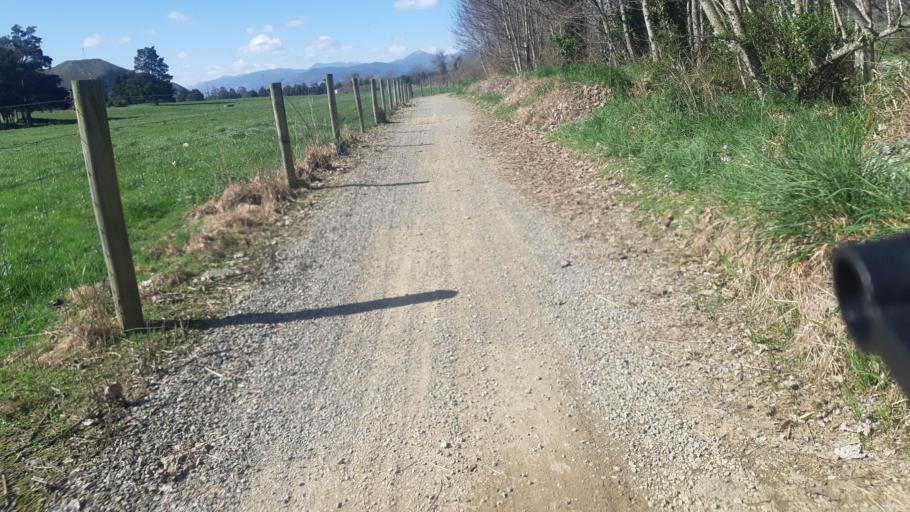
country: NZ
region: Tasman
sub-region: Tasman District
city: Wakefield
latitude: -41.4053
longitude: 173.0185
